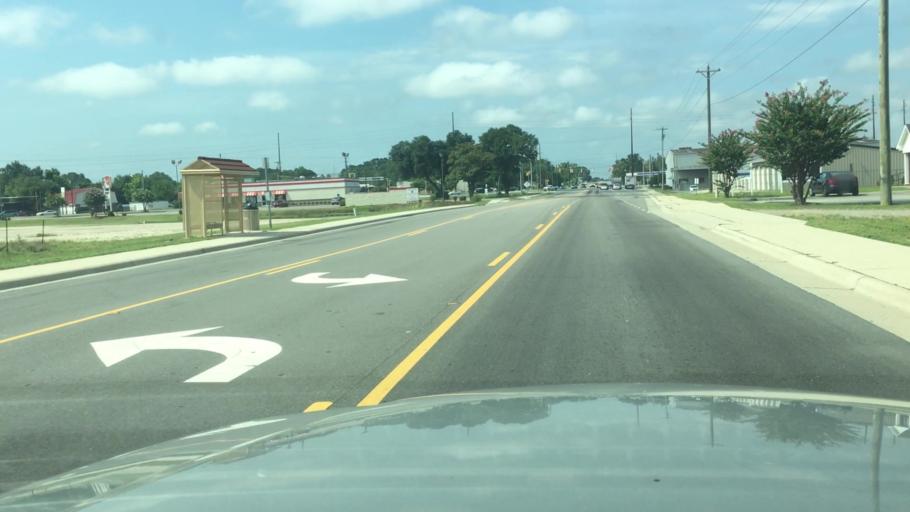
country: US
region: North Carolina
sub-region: Cumberland County
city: Fayetteville
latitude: 35.0206
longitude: -78.9023
